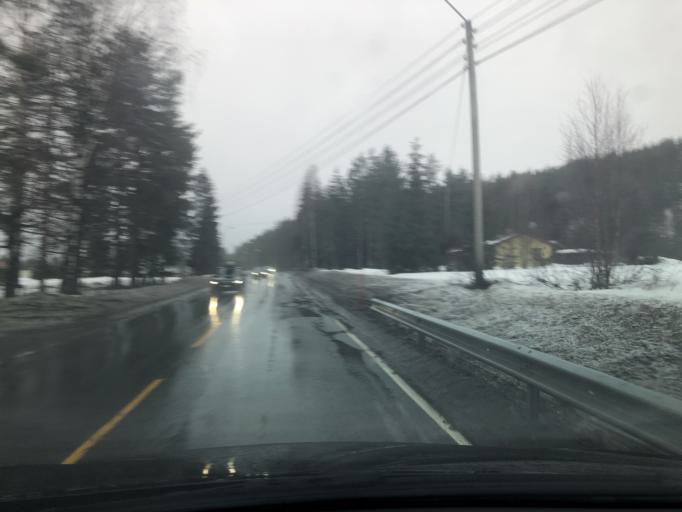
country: NO
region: Oppland
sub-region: Nordre Land
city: Dokka
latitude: 60.5721
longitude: 9.9811
